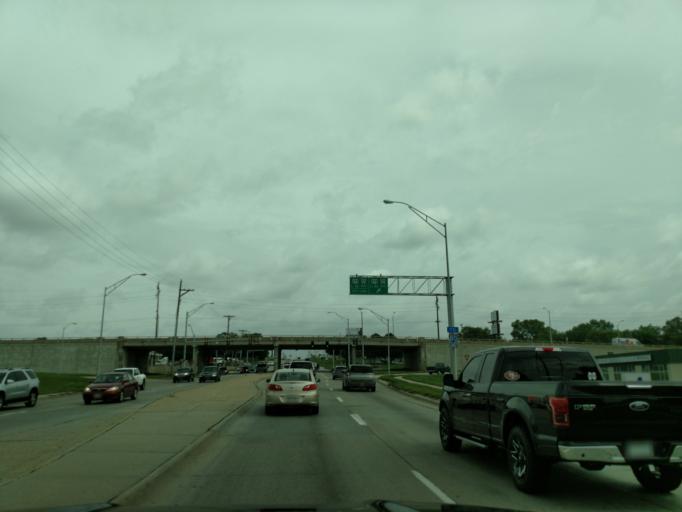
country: US
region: Nebraska
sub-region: Douglas County
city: Ralston
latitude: 41.2114
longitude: -96.0238
